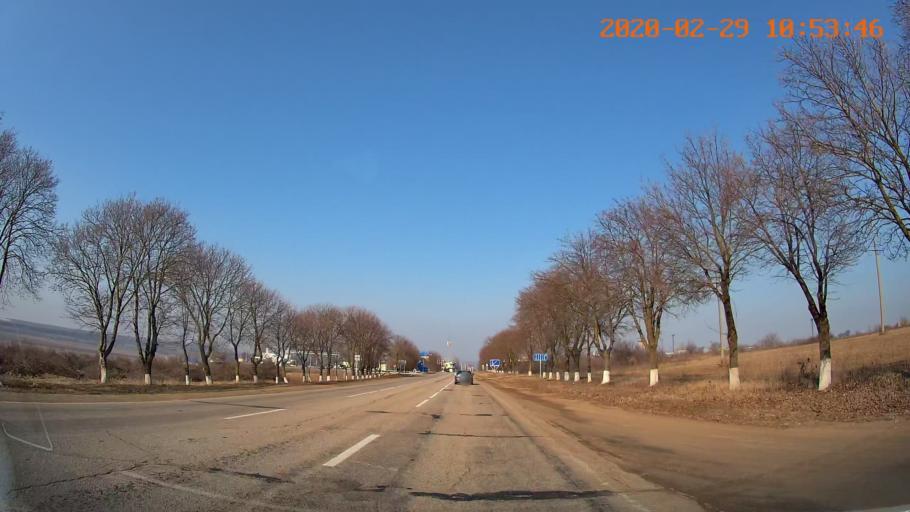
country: MD
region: Telenesti
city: Grigoriopol
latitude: 47.1183
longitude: 29.3313
